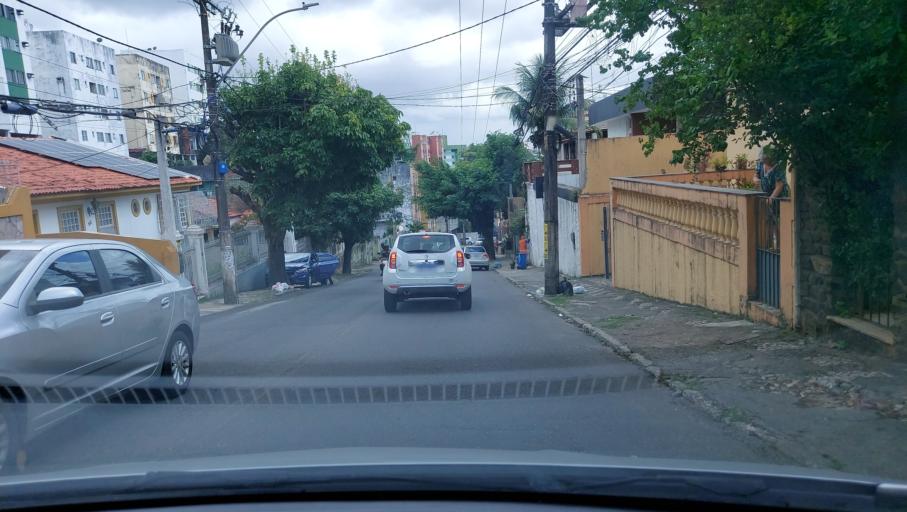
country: BR
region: Bahia
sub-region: Salvador
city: Salvador
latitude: -12.9711
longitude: -38.4905
